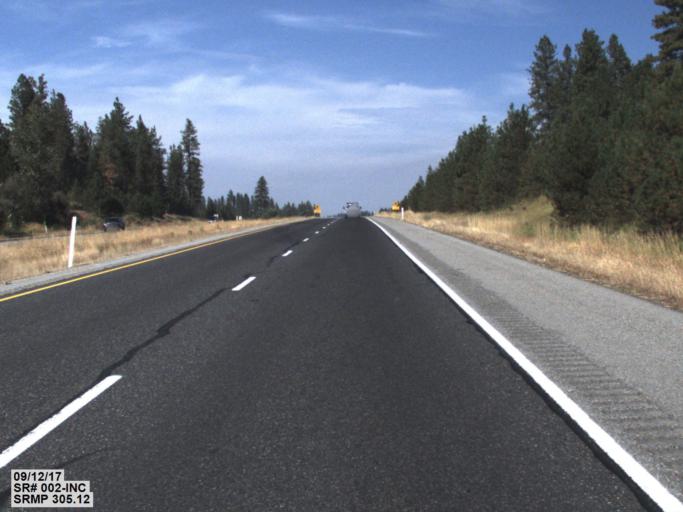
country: US
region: Washington
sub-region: Spokane County
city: Mead
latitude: 47.8984
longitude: -117.3520
